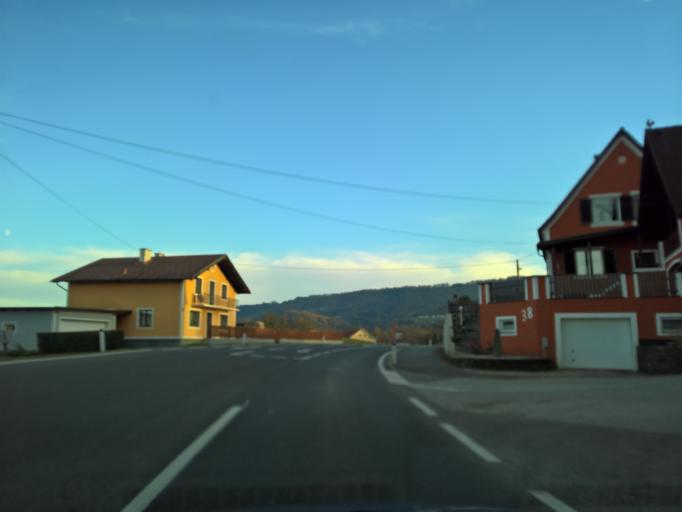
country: AT
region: Styria
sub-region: Politischer Bezirk Leibnitz
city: Arnfels
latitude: 46.6792
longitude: 15.3893
